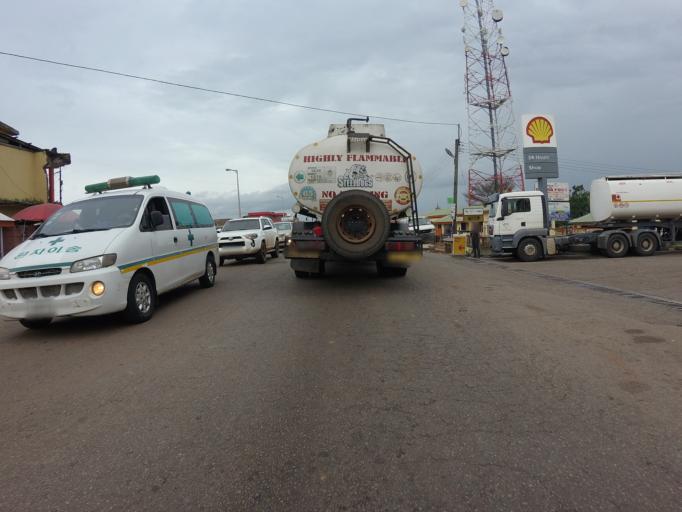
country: GH
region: Ashanti
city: Konongo
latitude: 6.6252
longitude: -1.2088
